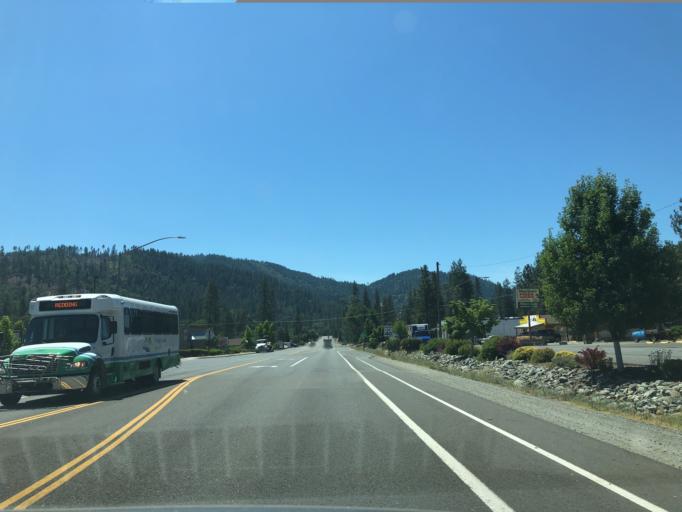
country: US
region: California
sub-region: Trinity County
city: Weaverville
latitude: 40.7221
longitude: -122.9292
